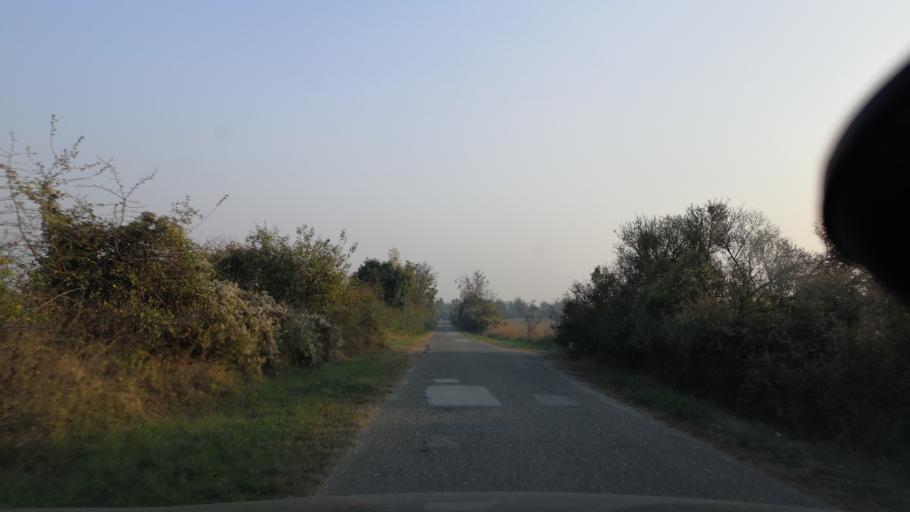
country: RS
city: Cortanovci
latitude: 45.1333
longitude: 19.9870
